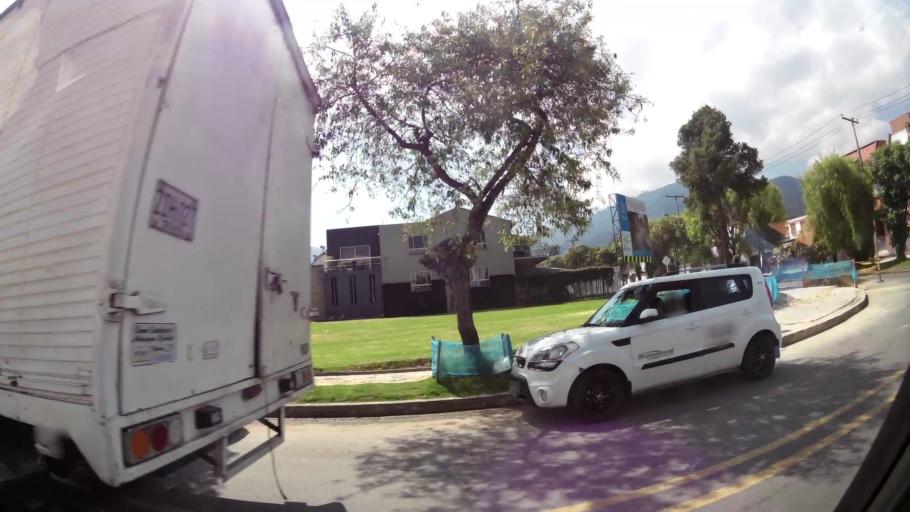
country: CO
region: Bogota D.C.
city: Barrio San Luis
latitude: 4.6900
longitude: -74.0368
